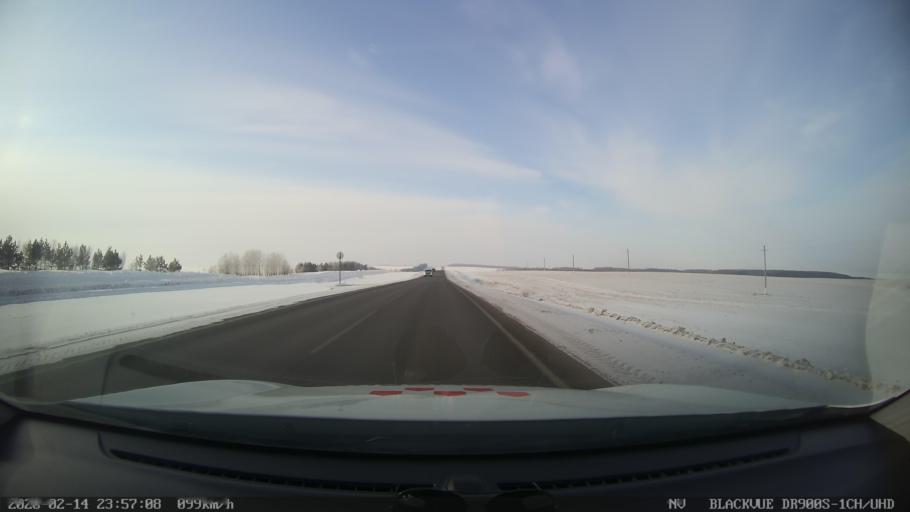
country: RU
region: Tatarstan
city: Kuybyshevskiy Zaton
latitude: 55.3317
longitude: 49.1168
